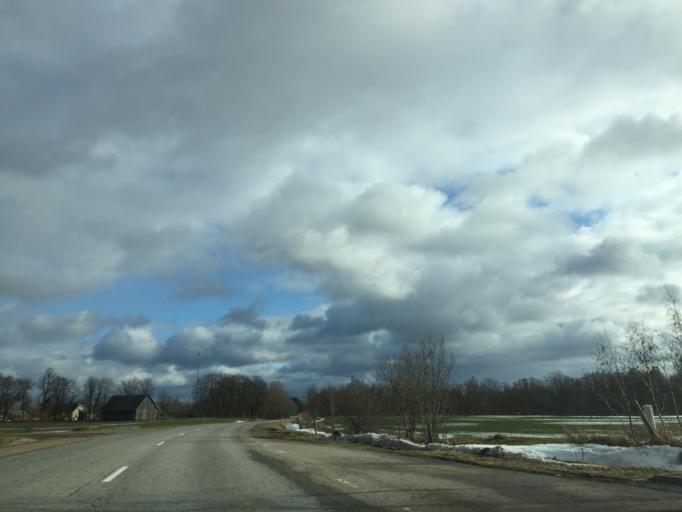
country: LV
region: Aloja
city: Staicele
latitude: 57.8944
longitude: 24.6361
